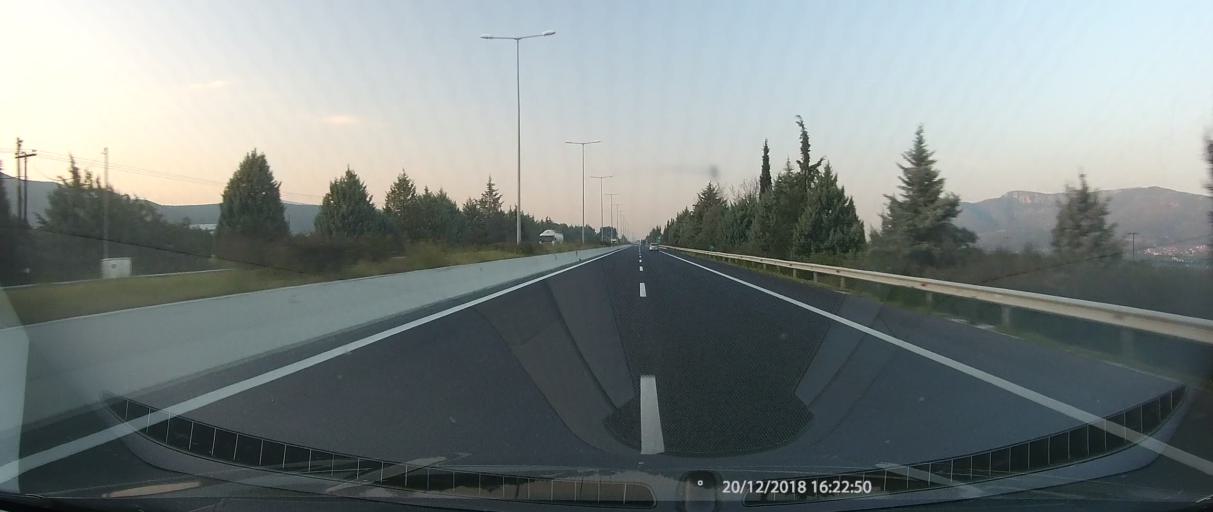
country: GR
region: Thessaly
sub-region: Nomos Magnisias
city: Sourpi
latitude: 39.0780
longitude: 22.8811
